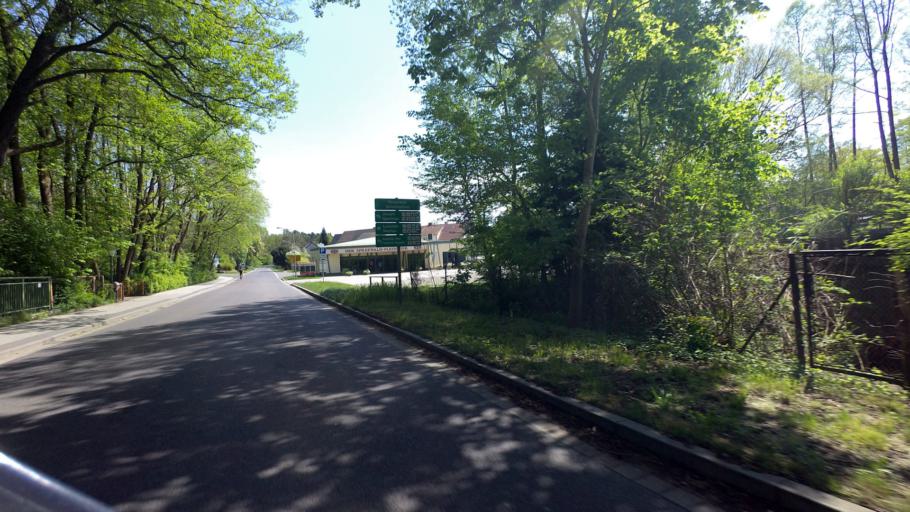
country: DE
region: Brandenburg
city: Neu Zauche
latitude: 52.0099
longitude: 14.1860
